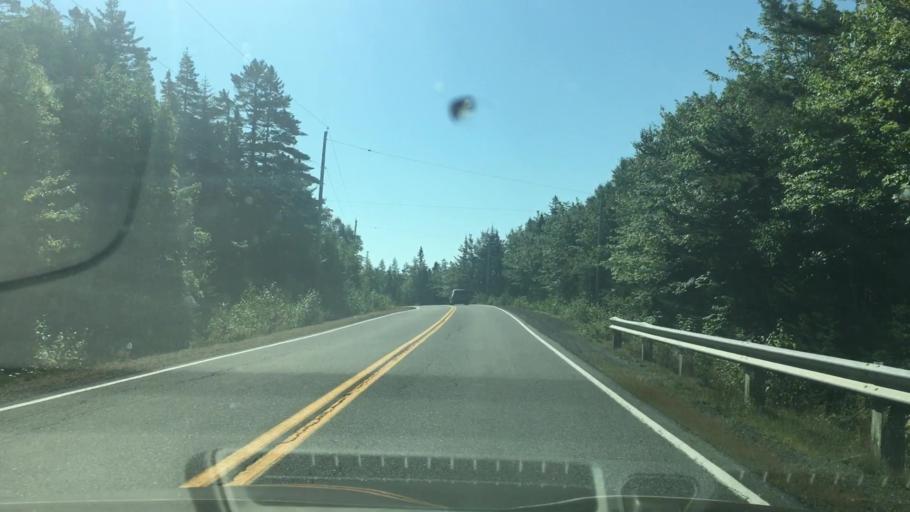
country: CA
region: Nova Scotia
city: Cole Harbour
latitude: 44.8091
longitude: -62.8347
